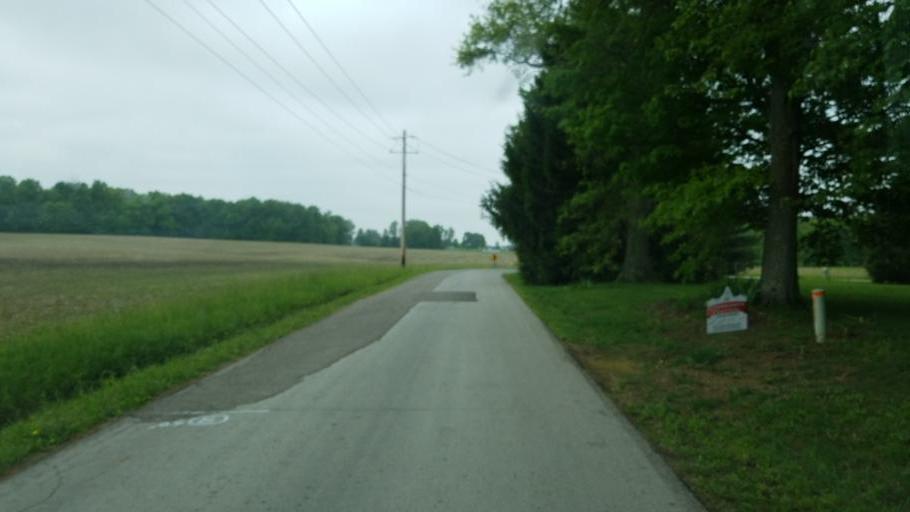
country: US
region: Ohio
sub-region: Knox County
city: Centerburg
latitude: 40.3071
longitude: -82.7475
